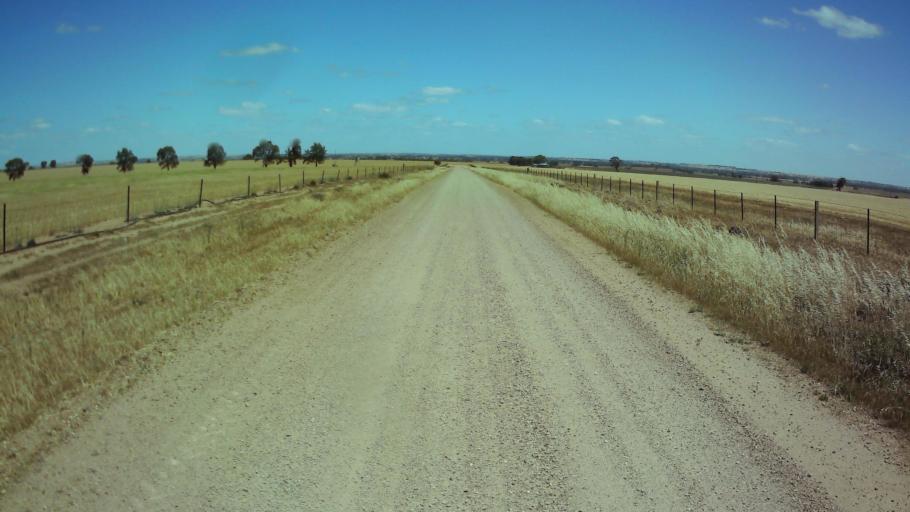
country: AU
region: New South Wales
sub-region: Weddin
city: Grenfell
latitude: -33.9647
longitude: 148.3307
